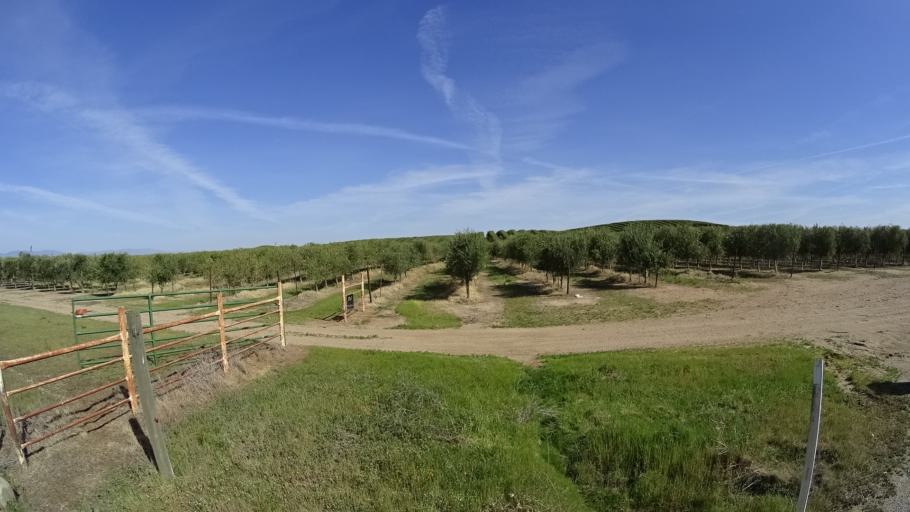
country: US
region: California
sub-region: Glenn County
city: Willows
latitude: 39.6151
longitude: -122.2935
